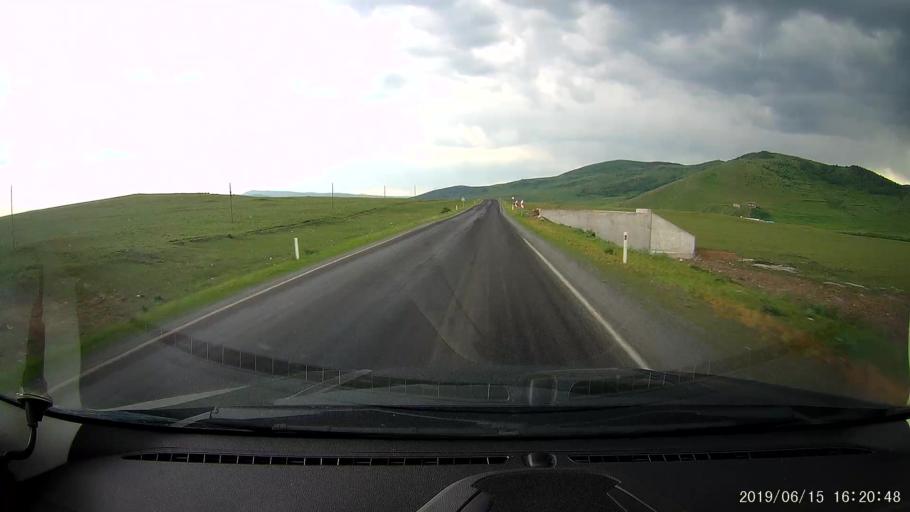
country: TR
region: Ardahan
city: Hanak
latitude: 41.2079
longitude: 42.8465
